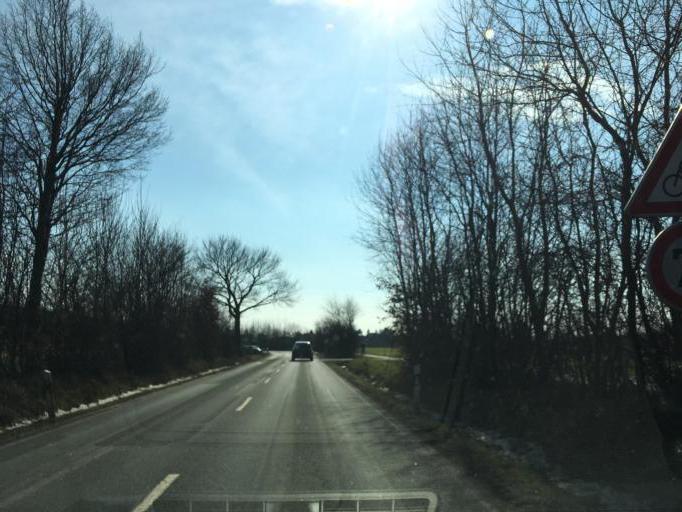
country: DE
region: Schleswig-Holstein
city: Escheburg
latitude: 53.4731
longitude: 10.3123
